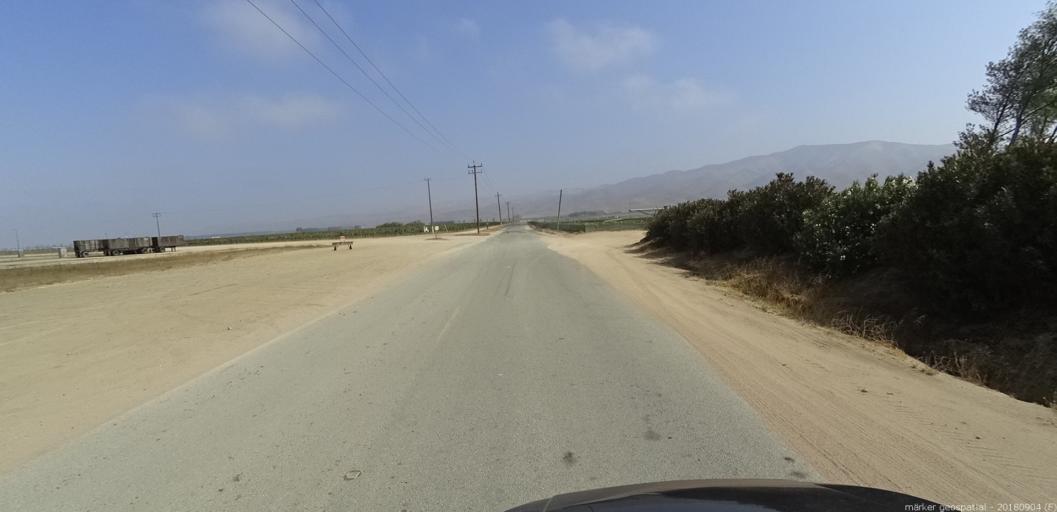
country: US
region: California
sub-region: Monterey County
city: Soledad
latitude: 36.4565
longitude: -121.3560
